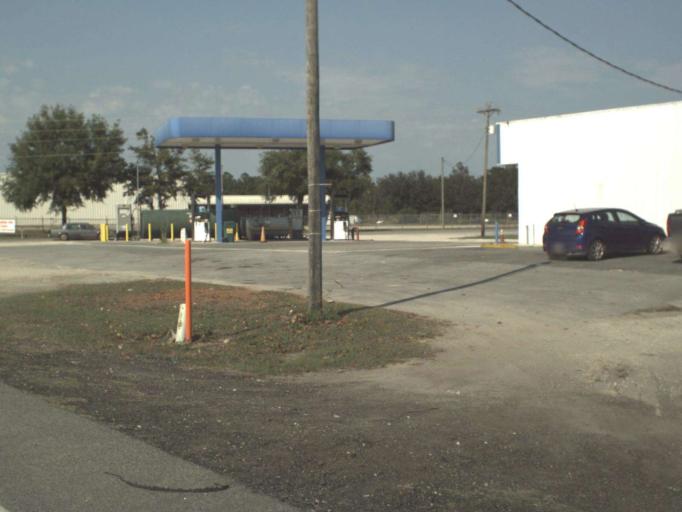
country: US
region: Florida
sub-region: Gulf County
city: Wewahitchka
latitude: 30.0403
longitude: -85.1844
